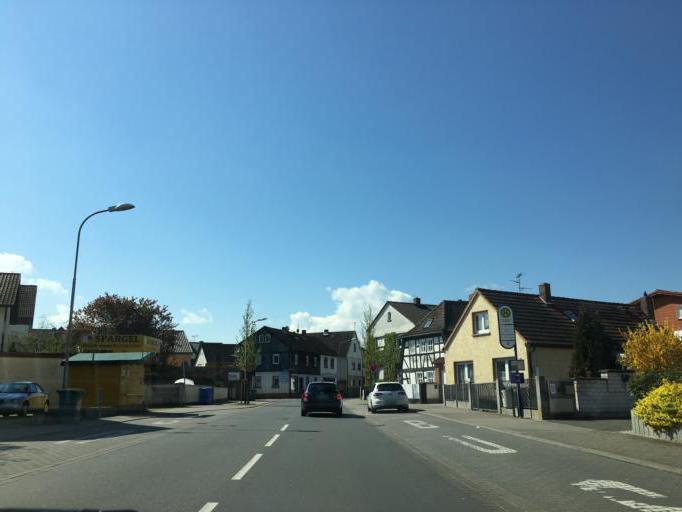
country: DE
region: Hesse
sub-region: Regierungsbezirk Darmstadt
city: Rodgau
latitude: 50.0050
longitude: 8.8905
